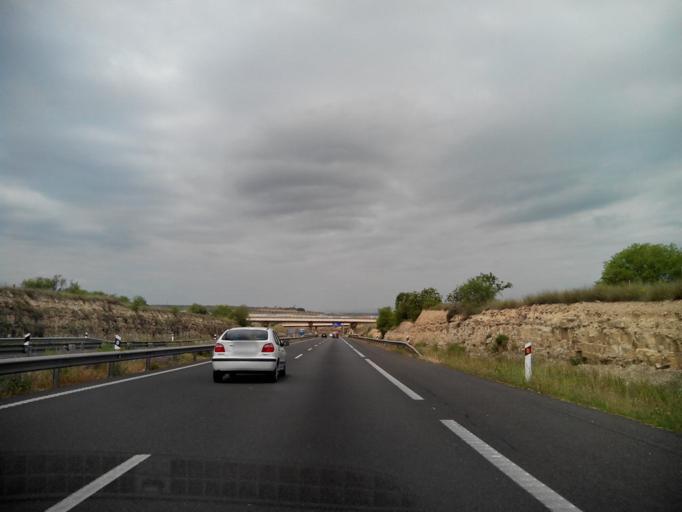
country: ES
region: Catalonia
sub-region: Provincia de Lleida
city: Tarrega
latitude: 41.6598
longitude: 1.1532
